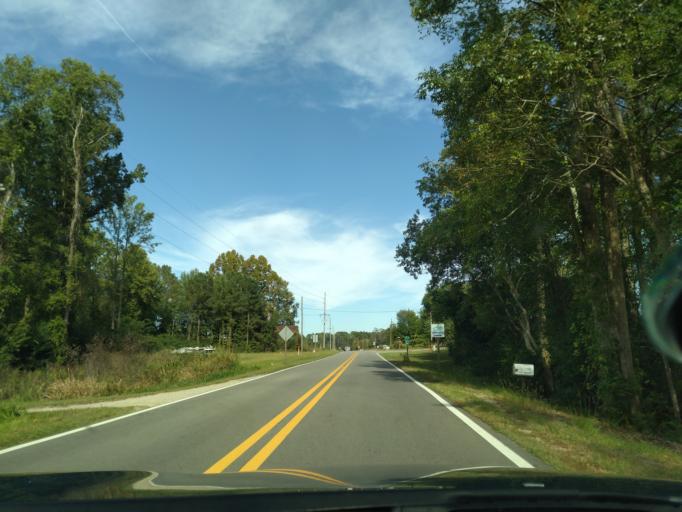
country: US
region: North Carolina
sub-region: Beaufort County
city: River Road
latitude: 35.5127
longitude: -76.9648
